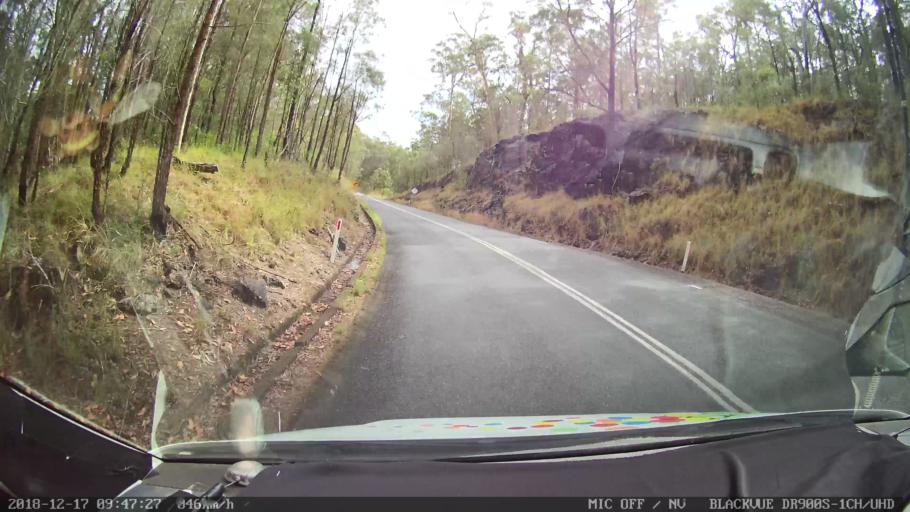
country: AU
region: New South Wales
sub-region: Tenterfield Municipality
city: Carrolls Creek
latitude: -28.9284
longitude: 152.3381
